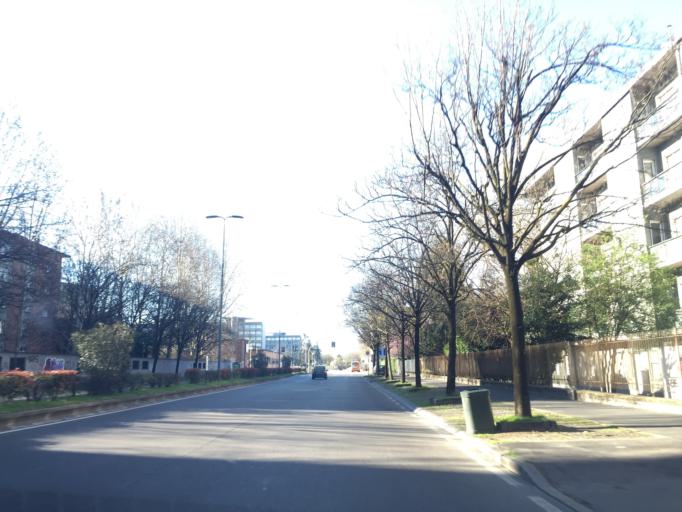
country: IT
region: Lombardy
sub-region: Citta metropolitana di Milano
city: Milano
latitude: 45.4388
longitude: 9.1876
